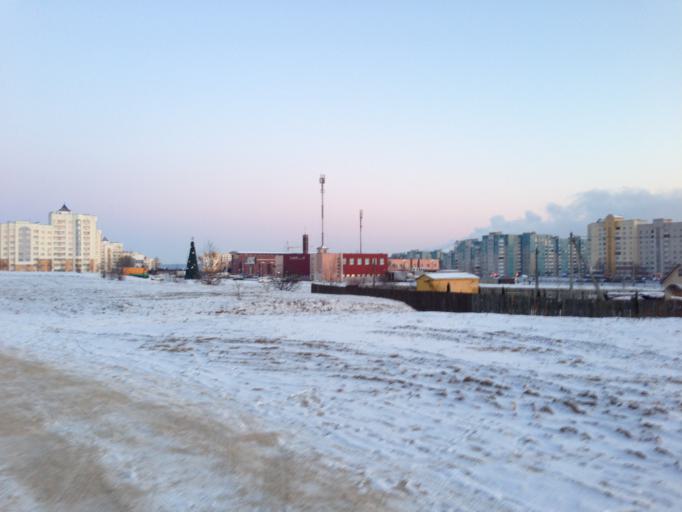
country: BY
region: Grodnenskaya
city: Hrodna
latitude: 53.7095
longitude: 23.8450
